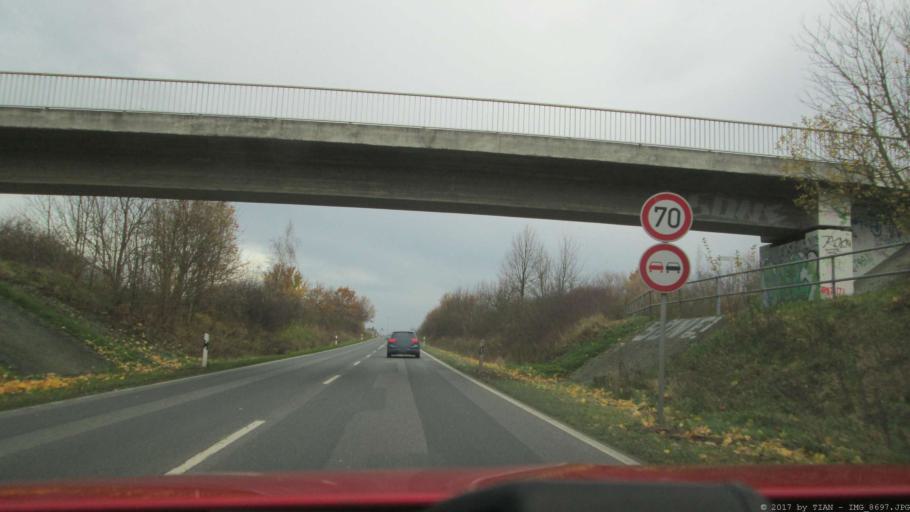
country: DE
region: Lower Saxony
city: Wolfsburg
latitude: 52.4418
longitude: 10.8255
